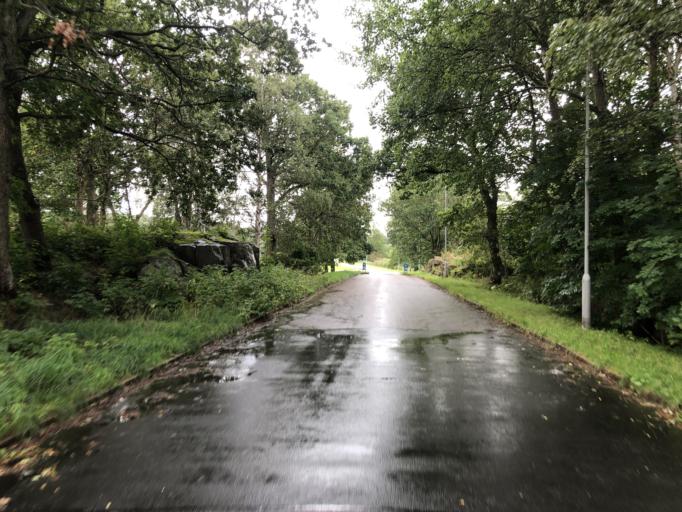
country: SE
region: Vaestra Goetaland
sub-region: Goteborg
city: Goeteborg
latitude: 57.7654
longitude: 11.9443
